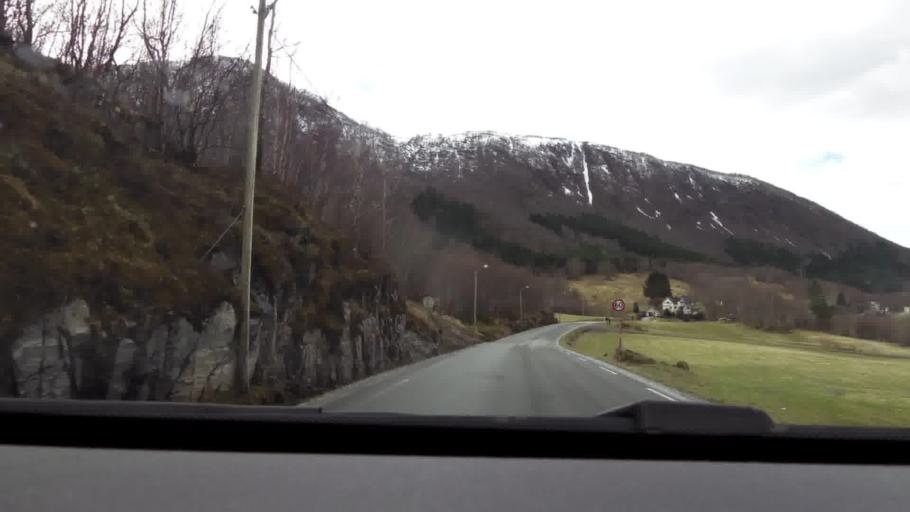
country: NO
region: More og Romsdal
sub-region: Kristiansund
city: Rensvik
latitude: 63.1107
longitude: 7.8036
